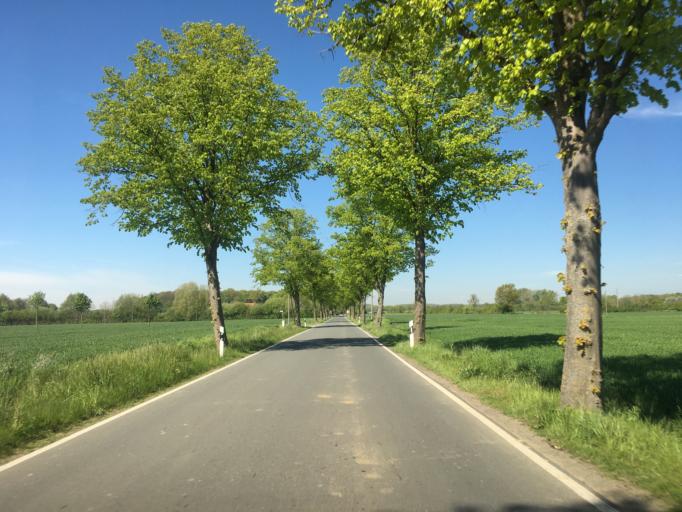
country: DE
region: North Rhine-Westphalia
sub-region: Regierungsbezirk Munster
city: Laer
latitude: 52.0198
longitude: 7.3698
